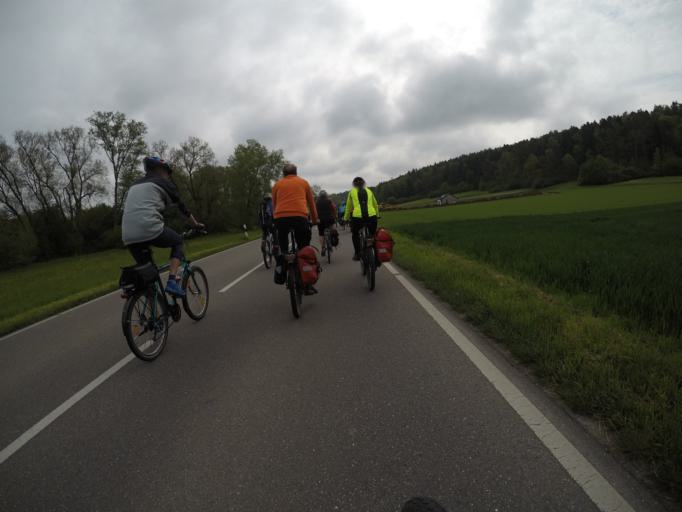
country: DE
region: Baden-Wuerttemberg
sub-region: Regierungsbezirk Stuttgart
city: Weil der Stadt
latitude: 48.7647
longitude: 8.8881
